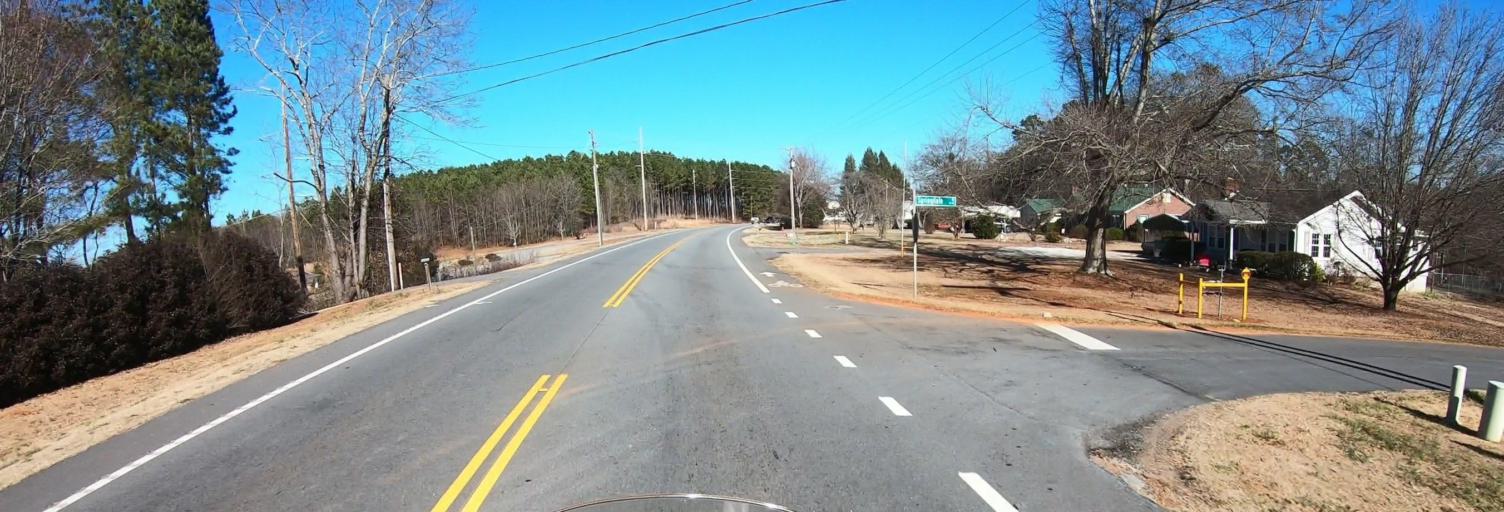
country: US
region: South Carolina
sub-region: Oconee County
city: Walhalla
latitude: 34.7724
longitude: -83.0311
